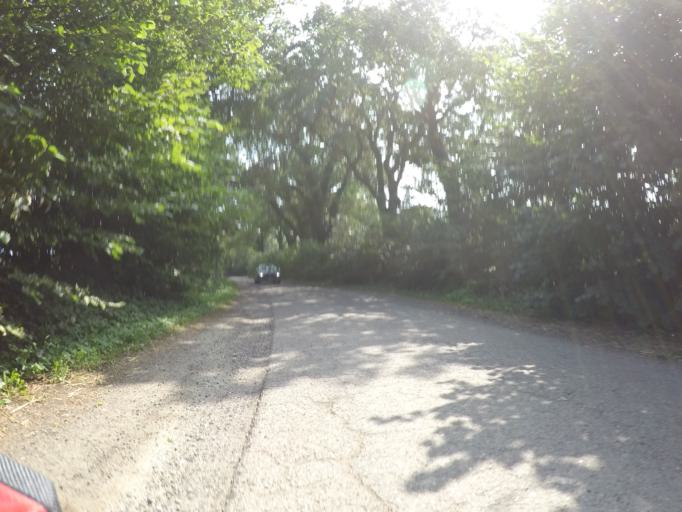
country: DE
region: Schleswig-Holstein
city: Kisdorf
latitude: 53.7984
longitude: 10.0171
